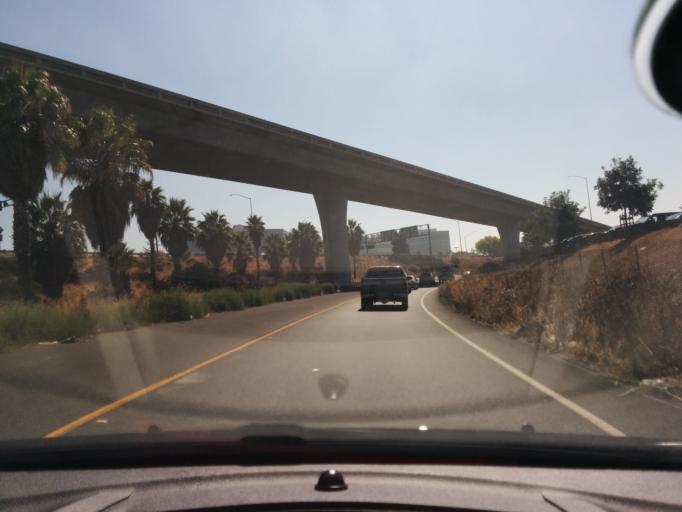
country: US
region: California
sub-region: Santa Clara County
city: Santa Clara
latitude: 37.3735
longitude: -121.9287
